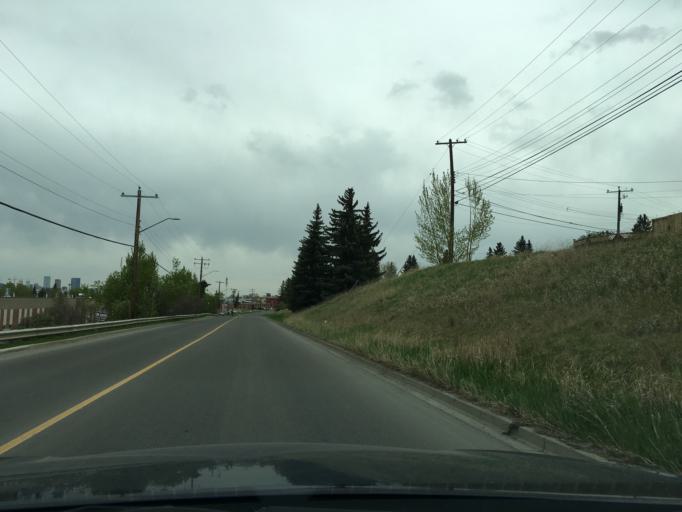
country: CA
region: Alberta
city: Calgary
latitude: 50.9833
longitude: -114.0689
